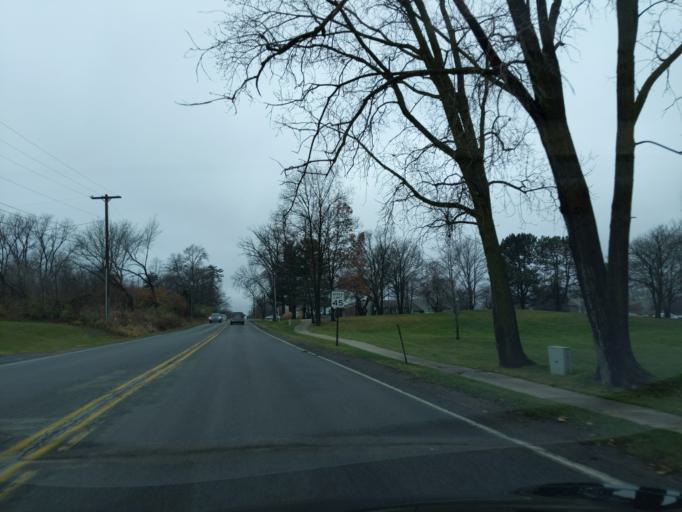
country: US
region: Michigan
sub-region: Jackson County
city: Jackson
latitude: 42.2766
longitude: -84.4548
